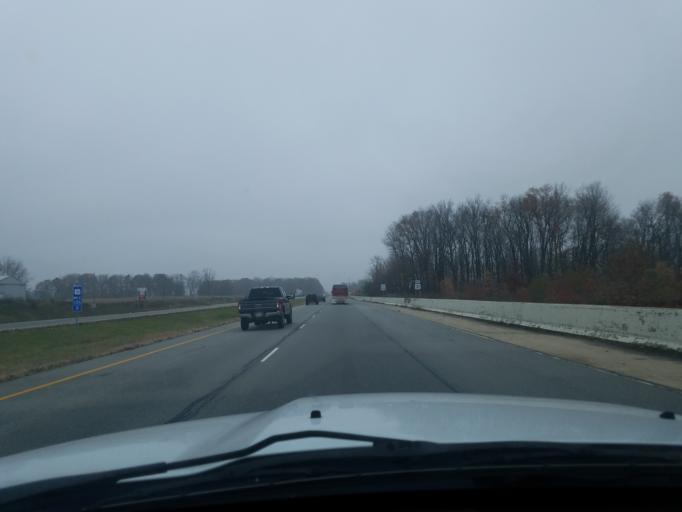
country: US
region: Indiana
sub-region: Hamilton County
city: Westfield
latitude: 40.0958
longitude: -86.1278
